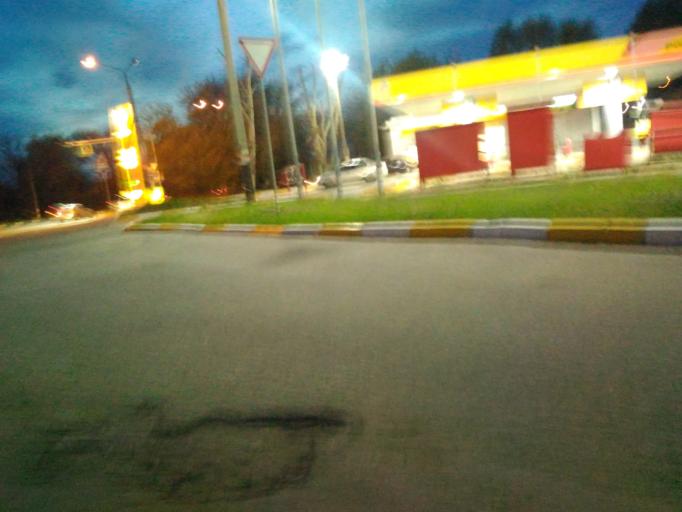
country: RU
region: Ulyanovsk
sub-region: Ulyanovskiy Rayon
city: Ulyanovsk
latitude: 54.2784
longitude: 48.3441
